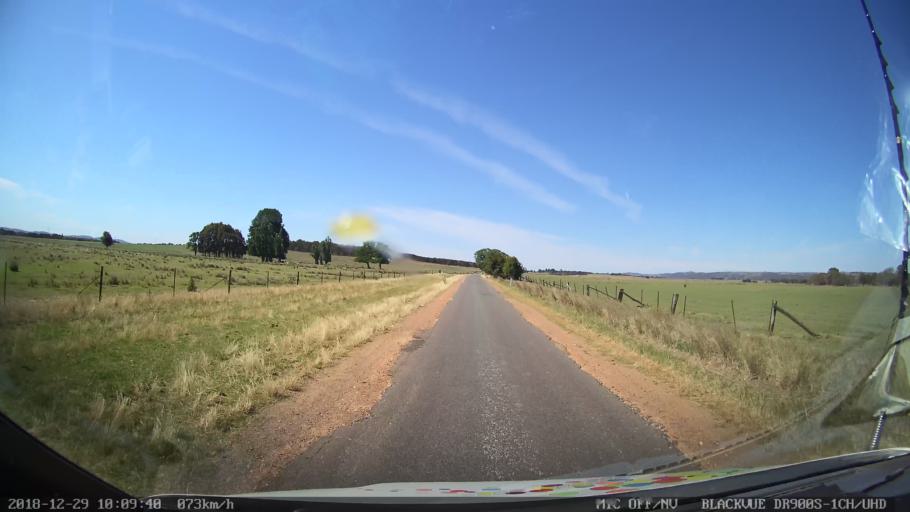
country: AU
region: New South Wales
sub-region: Yass Valley
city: Gundaroo
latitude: -34.8682
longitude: 149.4595
